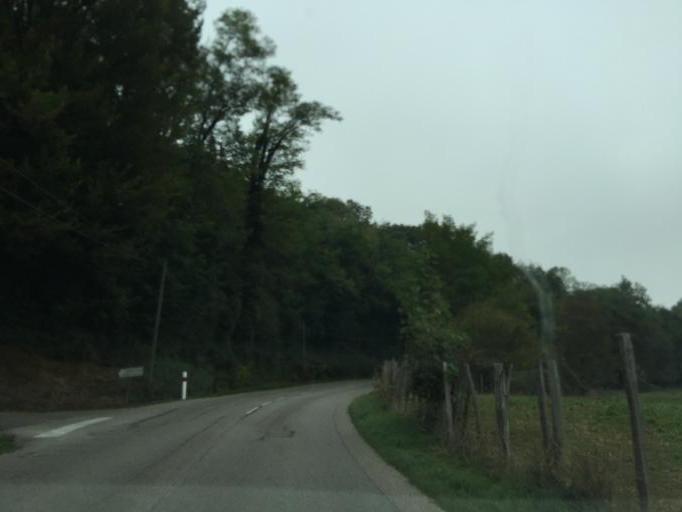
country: FR
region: Rhone-Alpes
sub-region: Departement de l'Isere
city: Saint-Clair-de-la-Tour
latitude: 45.5772
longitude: 5.4815
